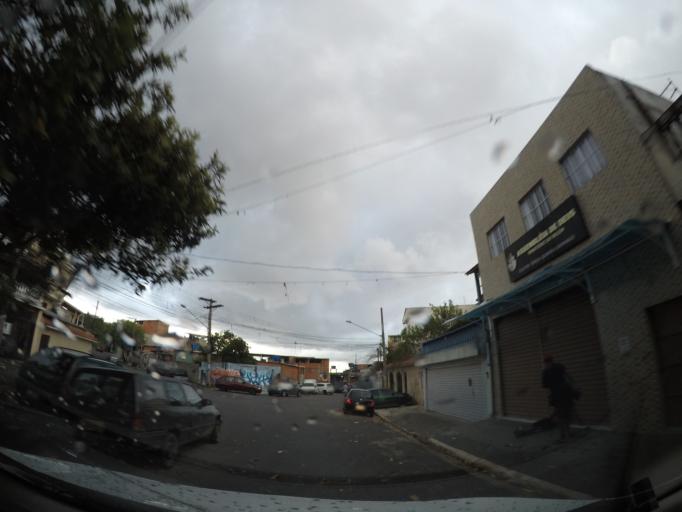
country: BR
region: Sao Paulo
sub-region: Guarulhos
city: Guarulhos
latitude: -23.4667
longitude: -46.5570
